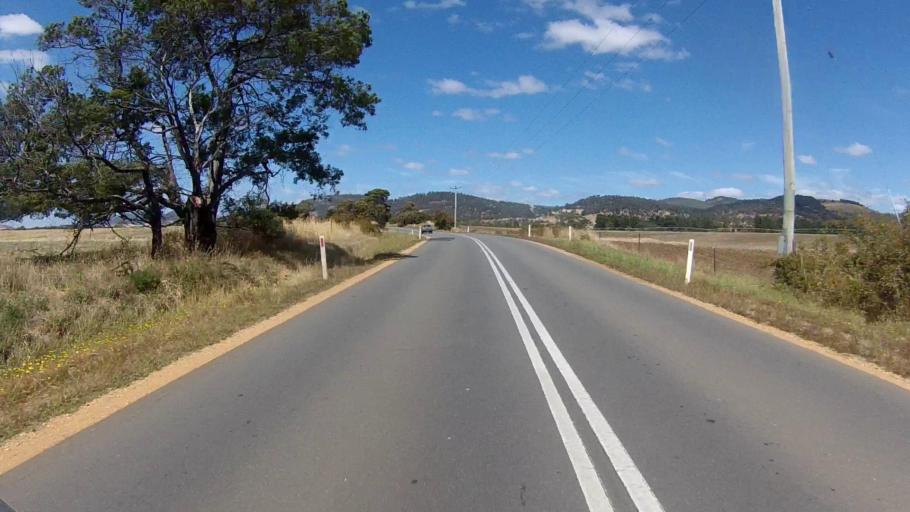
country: AU
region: Tasmania
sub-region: Clarence
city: Cambridge
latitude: -42.7621
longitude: 147.4152
